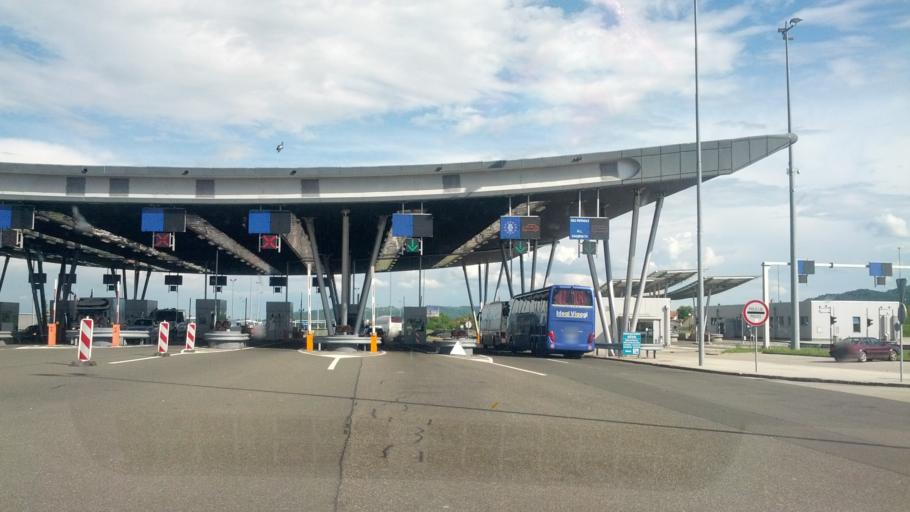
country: HR
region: Zagrebacka
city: Bregana
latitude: 45.8466
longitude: 15.6927
